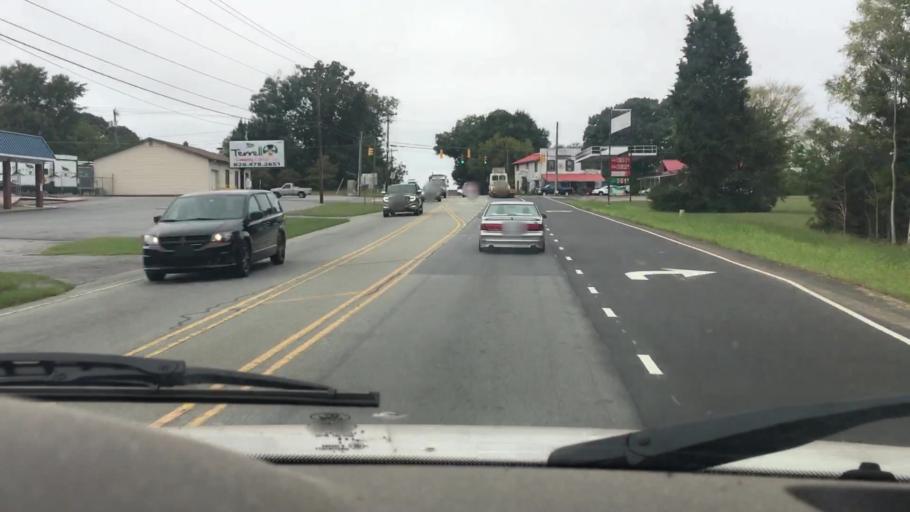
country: US
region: North Carolina
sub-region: Catawba County
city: Lake Norman of Catawba
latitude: 35.5896
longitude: -80.9764
